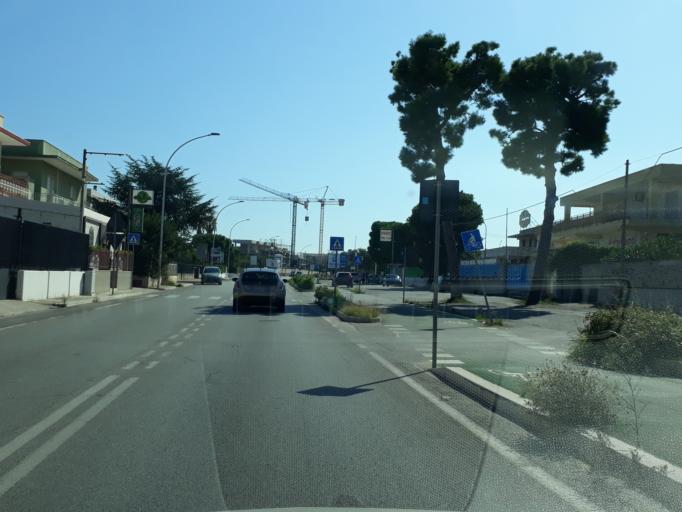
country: IT
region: Apulia
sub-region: Provincia di Bari
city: Monopoli
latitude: 40.9402
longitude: 17.3064
